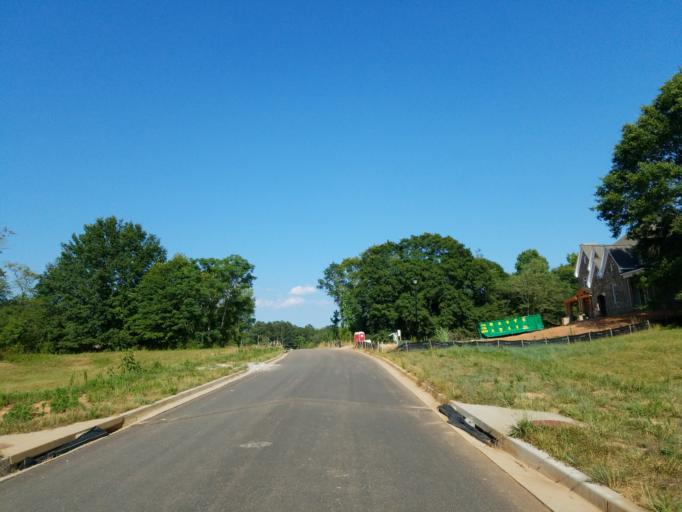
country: US
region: Georgia
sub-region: Fulton County
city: Milton
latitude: 34.1763
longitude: -84.3305
